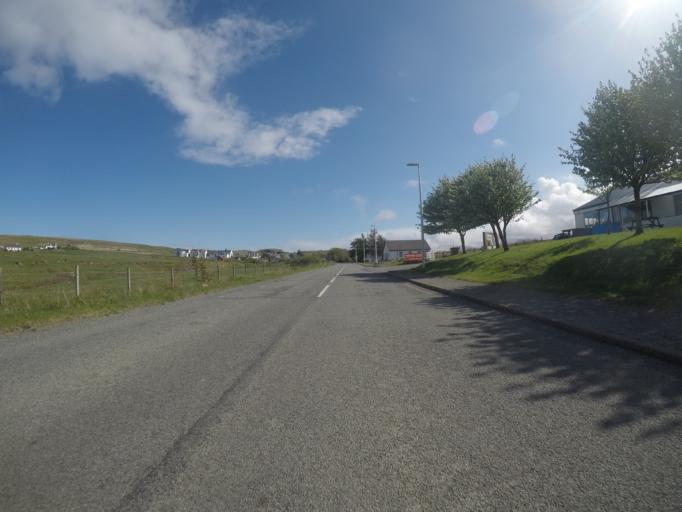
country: GB
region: Scotland
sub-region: Highland
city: Portree
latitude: 57.6286
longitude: -6.2099
